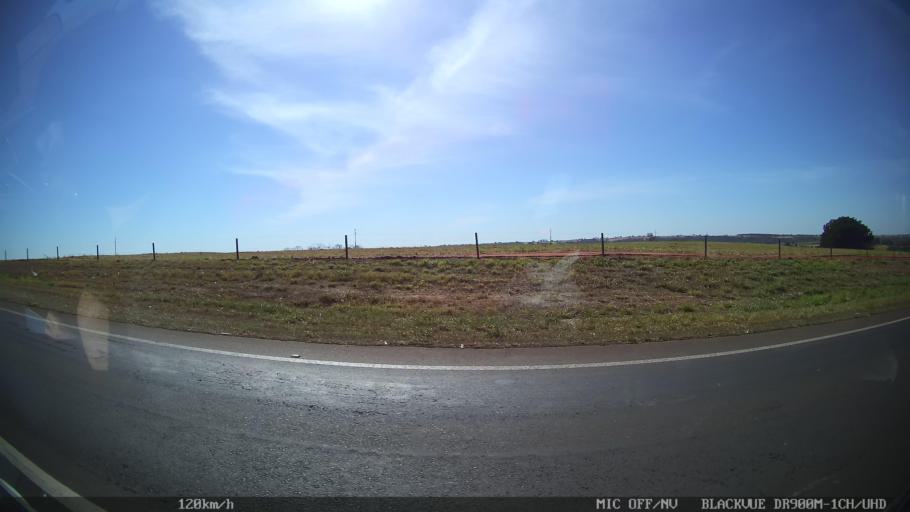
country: BR
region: Sao Paulo
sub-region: Olimpia
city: Olimpia
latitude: -20.6240
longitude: -48.7782
